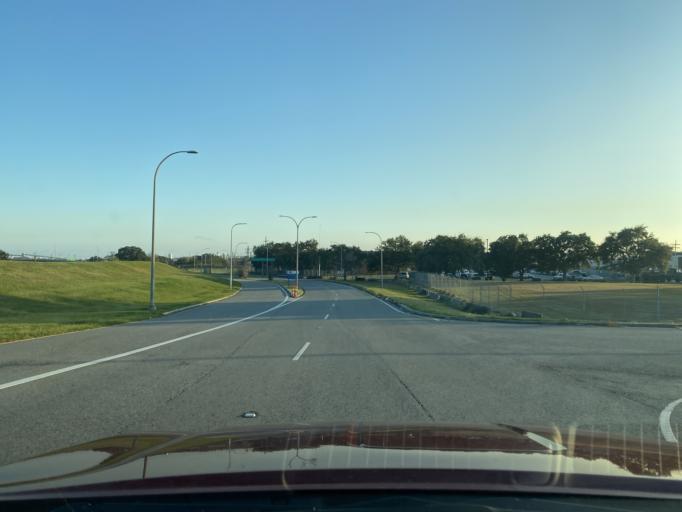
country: US
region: Louisiana
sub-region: Orleans Parish
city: New Orleans
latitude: 30.0330
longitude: -90.0413
